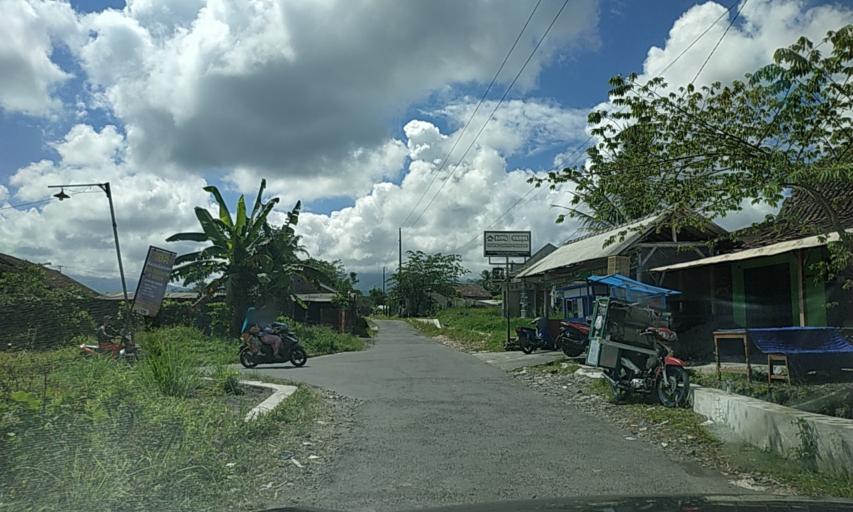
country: ID
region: Central Java
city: Muntilan
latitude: -7.5416
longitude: 110.3373
